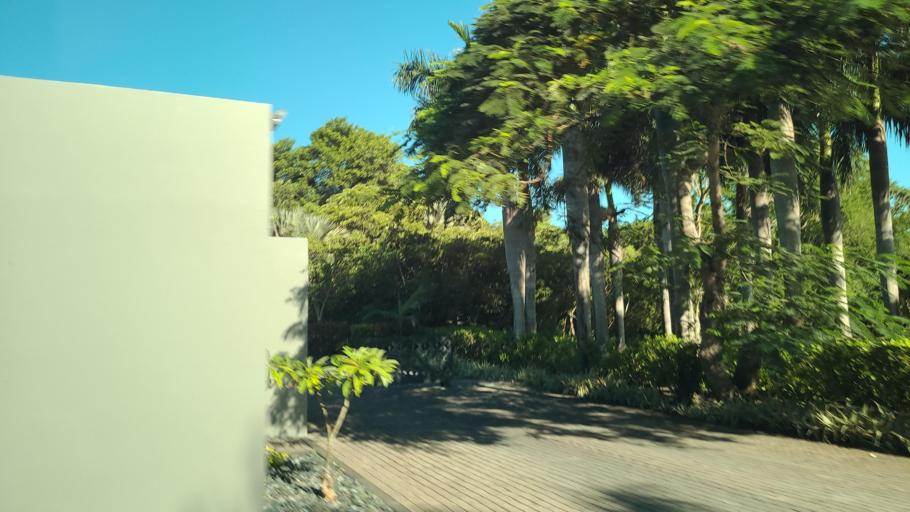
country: MU
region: Flacq
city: Mare La Chaux
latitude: -20.1704
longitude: 57.7676
